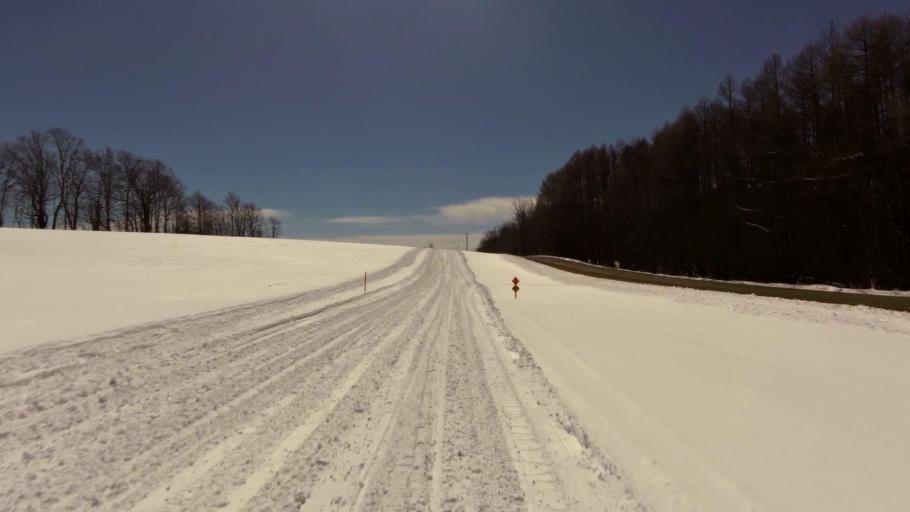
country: US
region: New York
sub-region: Allegany County
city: Houghton
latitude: 42.3532
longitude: -78.2606
